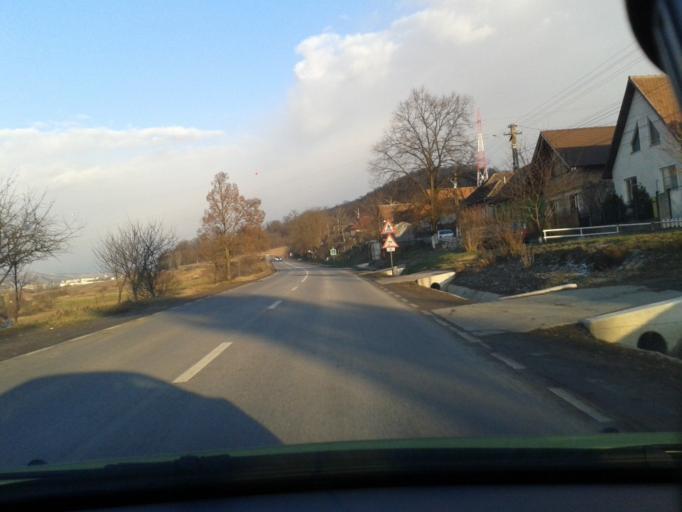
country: RO
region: Sibiu
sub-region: Comuna Tarnava
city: Tarnava
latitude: 46.1359
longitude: 24.3059
